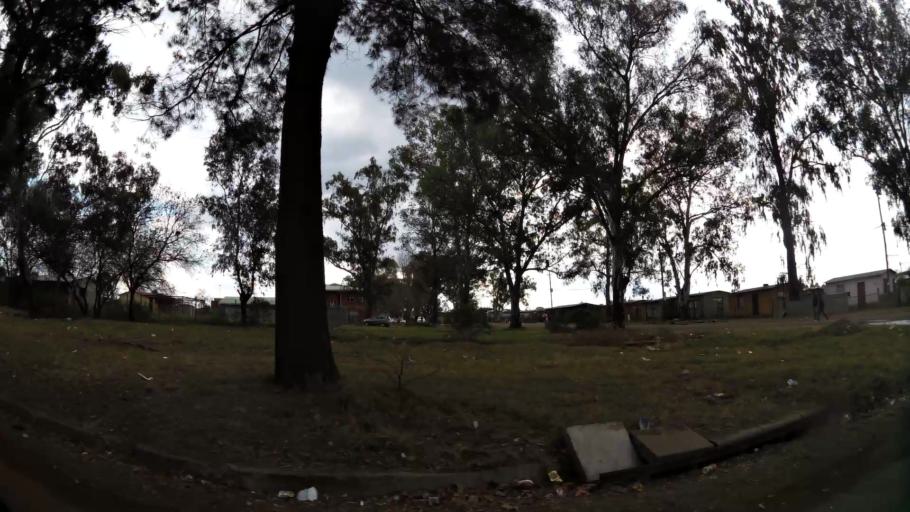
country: ZA
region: Gauteng
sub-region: Sedibeng District Municipality
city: Vanderbijlpark
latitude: -26.6700
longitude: 27.8444
